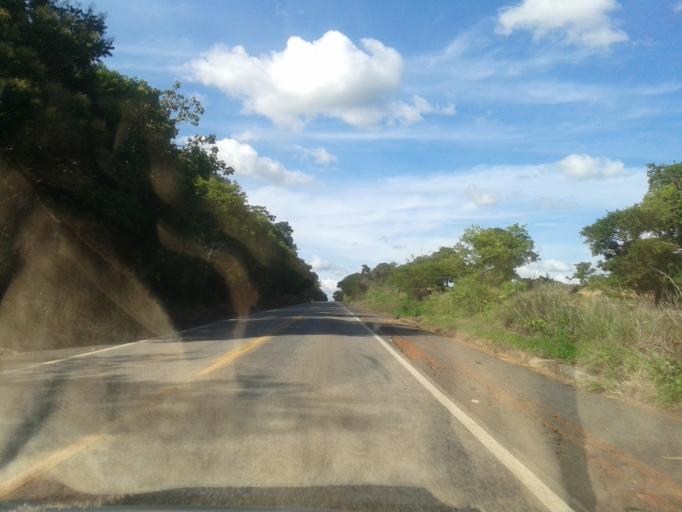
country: BR
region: Goias
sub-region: Mozarlandia
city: Mozarlandia
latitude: -14.9797
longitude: -50.5809
